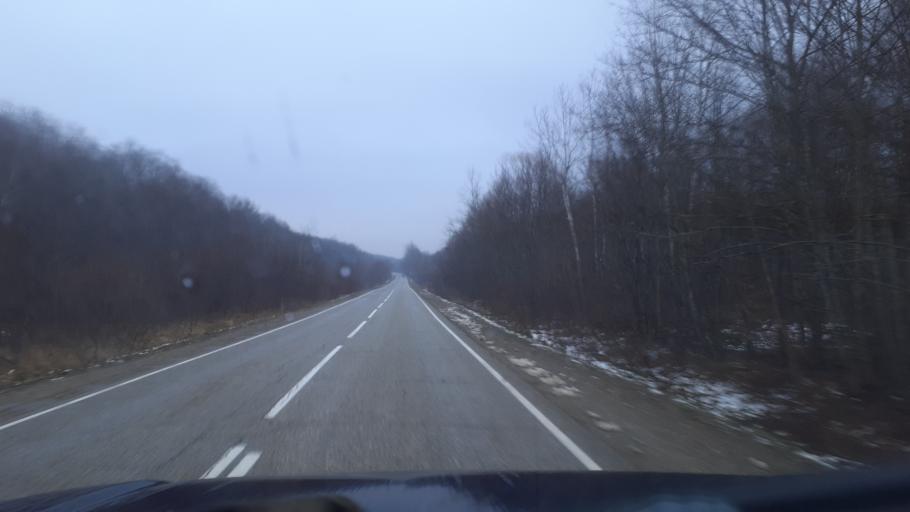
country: RU
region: Krasnodarskiy
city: Neftegorsk
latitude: 44.2778
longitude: 39.7935
